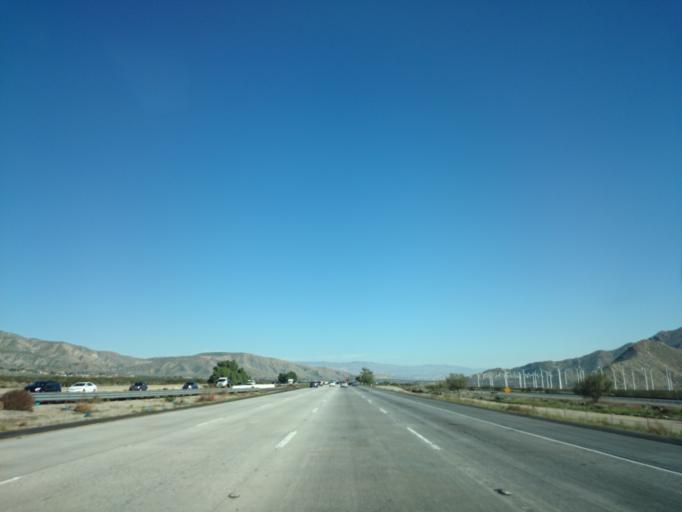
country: US
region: California
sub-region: Riverside County
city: Cabazon
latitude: 33.9209
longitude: -116.7536
